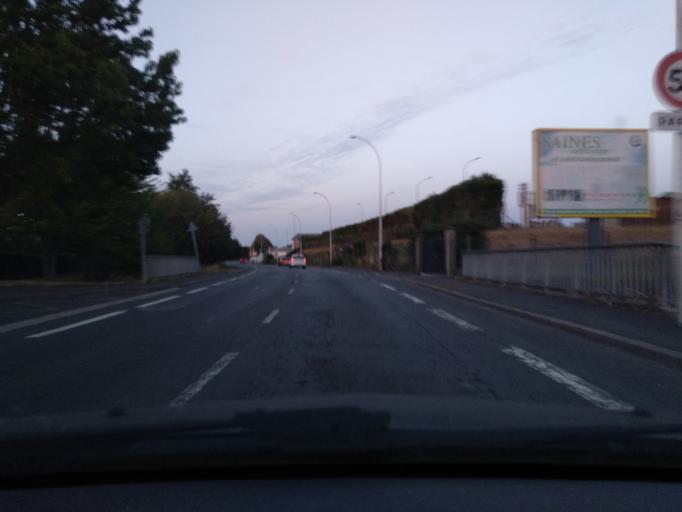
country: FR
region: Centre
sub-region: Departement d'Indre-et-Loire
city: Saint-Cyr-sur-Loire
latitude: 47.4328
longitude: 0.6863
